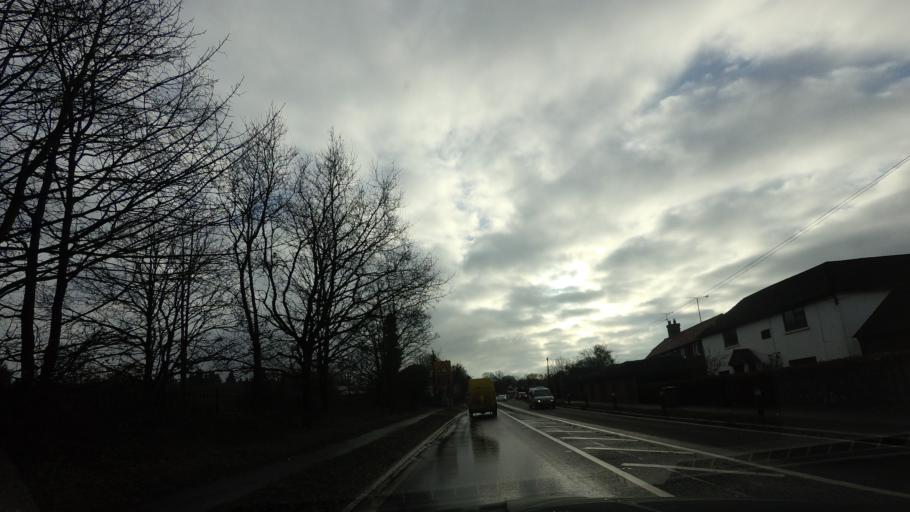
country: GB
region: England
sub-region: Kent
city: Hawkhurst
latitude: 51.0583
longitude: 0.4470
